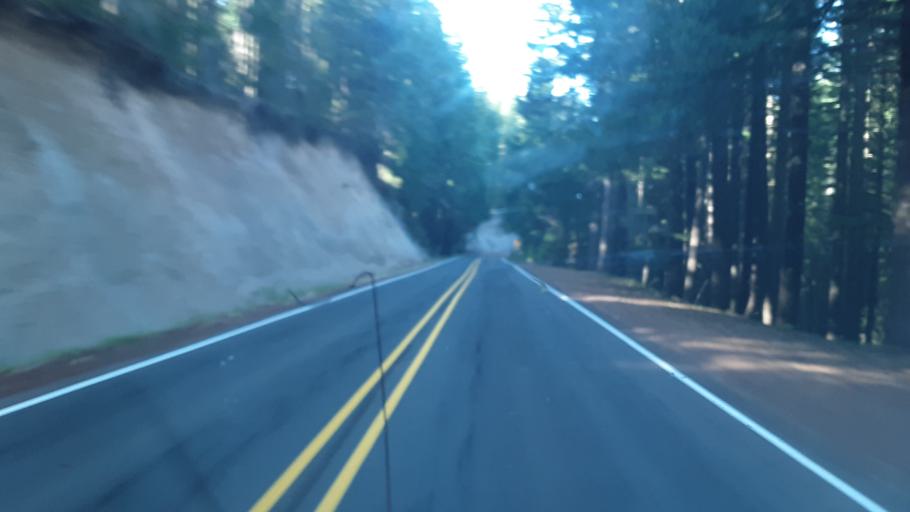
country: US
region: Oregon
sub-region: Jackson County
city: Shady Cove
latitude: 42.9382
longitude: -122.4196
